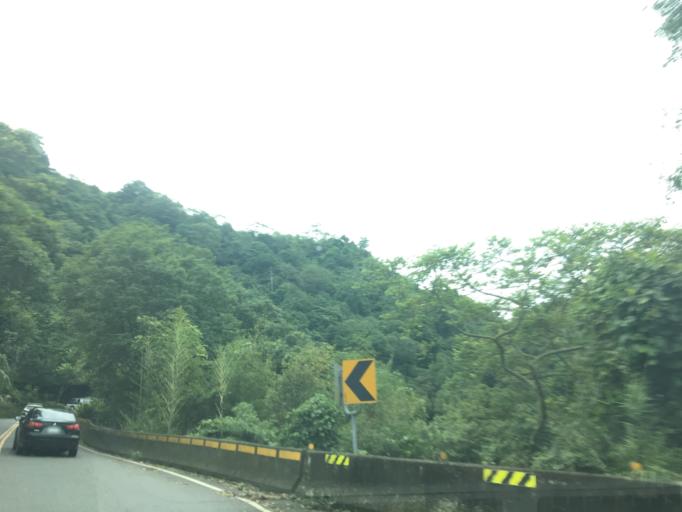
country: TW
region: Taiwan
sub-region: Yunlin
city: Douliu
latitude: 23.5621
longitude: 120.5956
